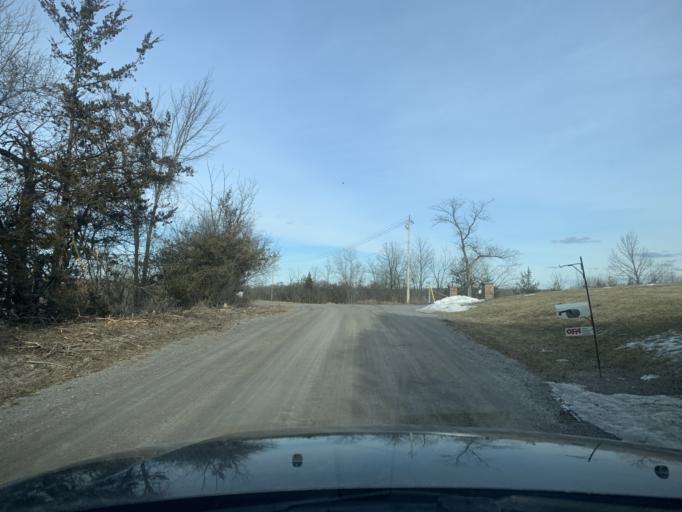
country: CA
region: Ontario
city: Deseronto
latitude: 44.3999
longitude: -77.1335
